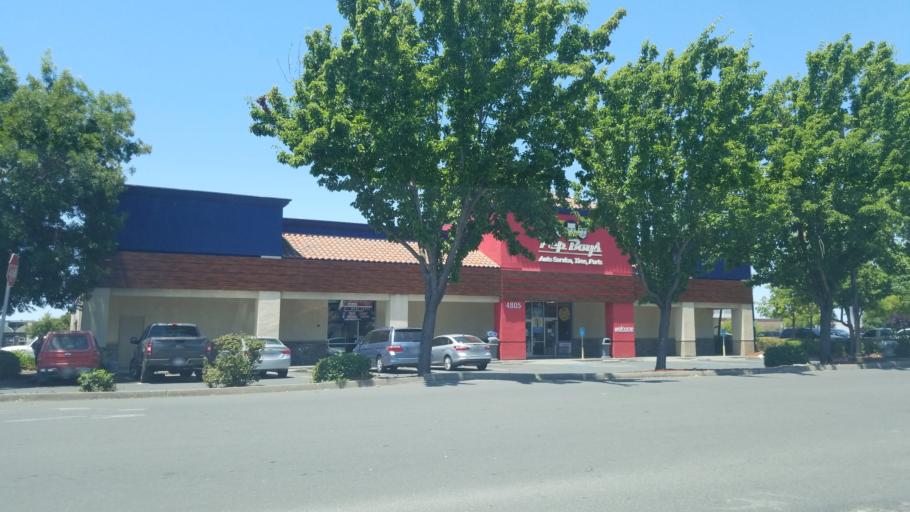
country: US
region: California
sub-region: Sonoma County
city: Rohnert Park
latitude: 38.3660
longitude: -122.7142
